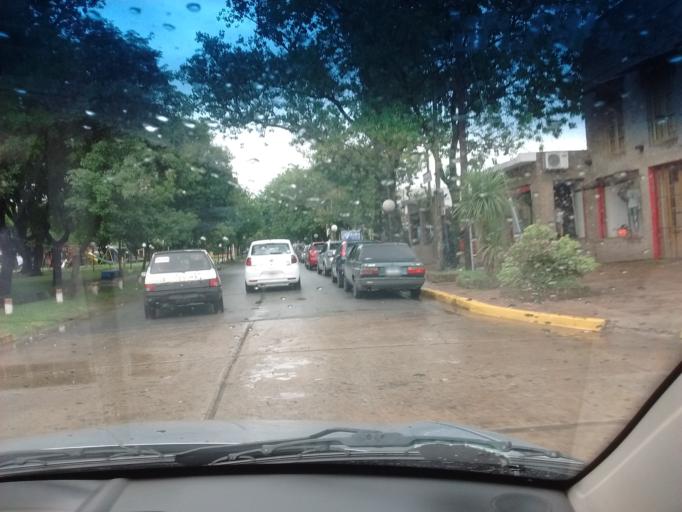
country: AR
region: Santa Fe
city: Funes
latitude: -32.9205
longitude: -60.8107
